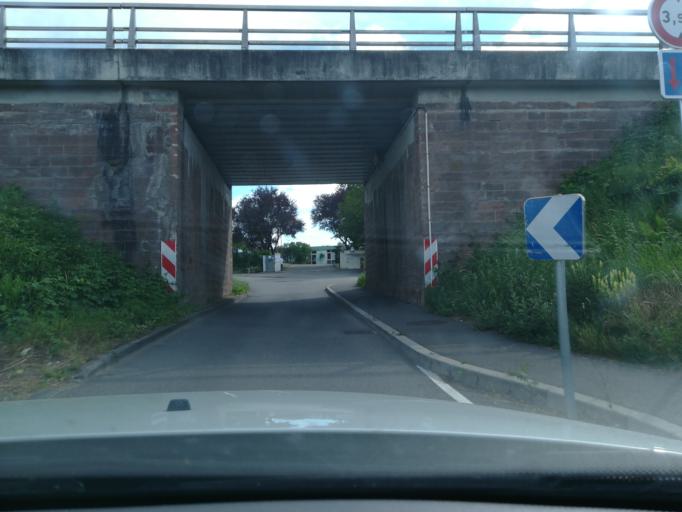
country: FR
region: Alsace
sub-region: Departement du Bas-Rhin
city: Ingwiller
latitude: 48.8645
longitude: 7.4822
